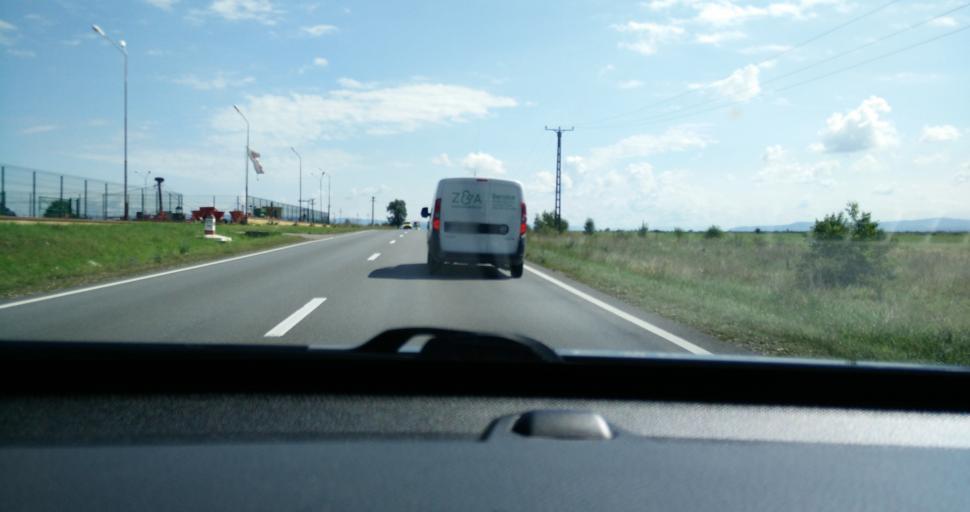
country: RO
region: Bihor
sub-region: Comuna Ineu
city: Ineu
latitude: 47.0567
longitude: 22.1122
